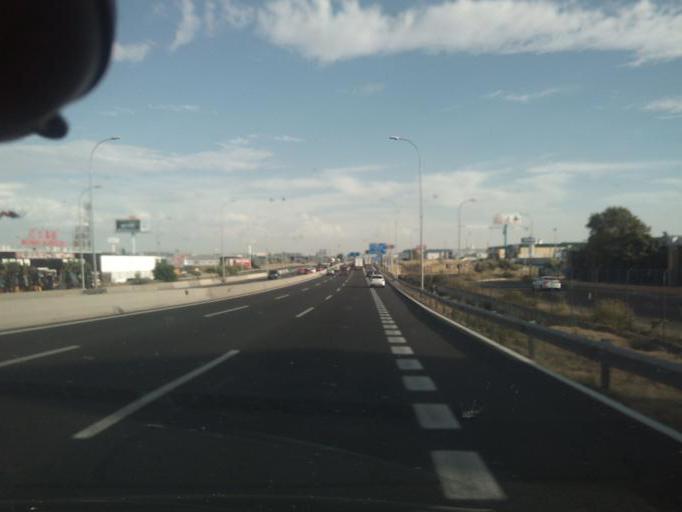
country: ES
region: Madrid
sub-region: Provincia de Madrid
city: Valdemoro
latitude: 40.1725
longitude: -3.6665
